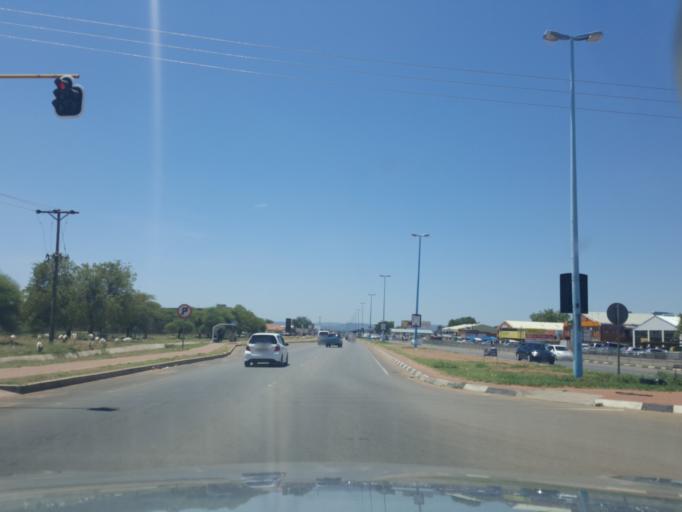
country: BW
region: Kweneng
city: Mogoditshane
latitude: -24.6121
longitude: 25.8611
